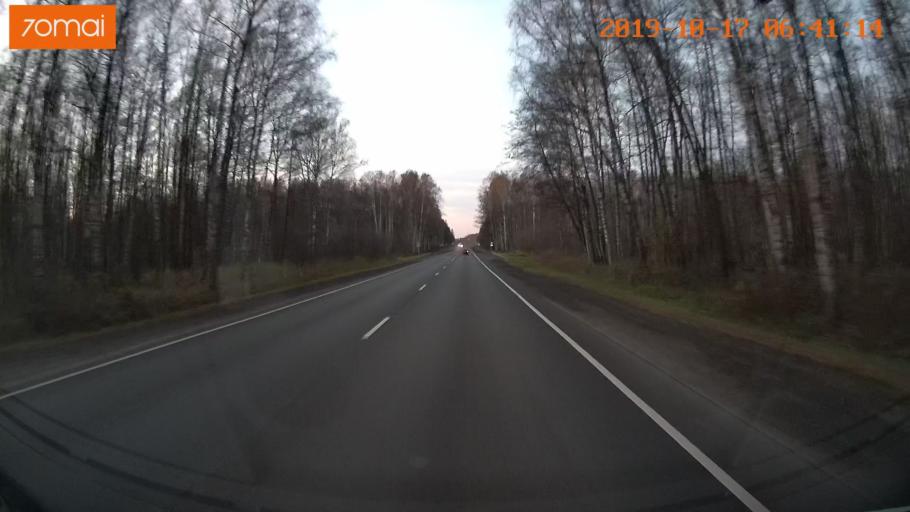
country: RU
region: Ivanovo
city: Nerl'
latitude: 56.6178
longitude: 40.5620
